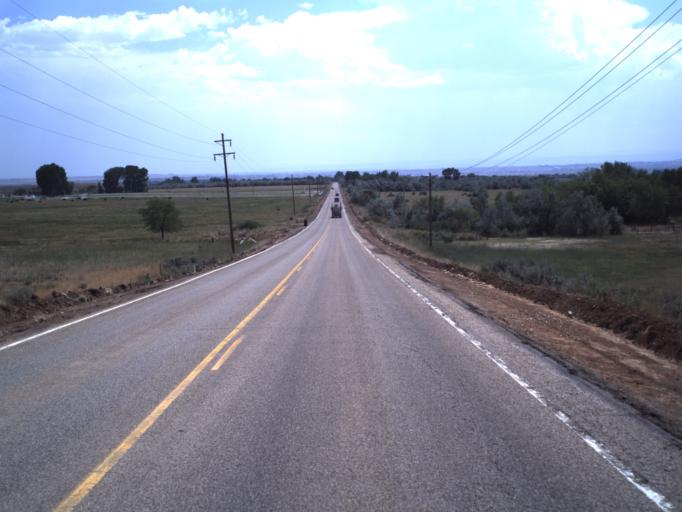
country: US
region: Utah
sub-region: Duchesne County
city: Roosevelt
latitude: 40.3689
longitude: -110.0297
